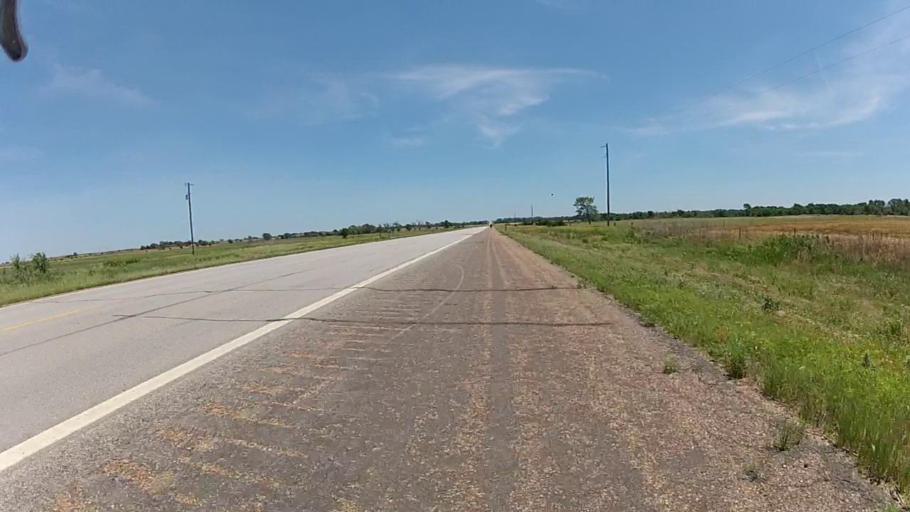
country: US
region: Kansas
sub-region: Barber County
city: Medicine Lodge
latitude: 37.2536
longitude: -98.3218
